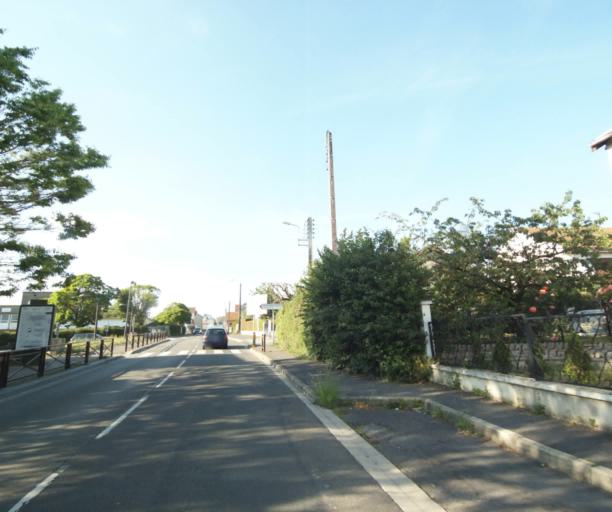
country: FR
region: Champagne-Ardenne
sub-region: Departement des Ardennes
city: Charleville-Mezieres
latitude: 49.7856
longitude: 4.7132
